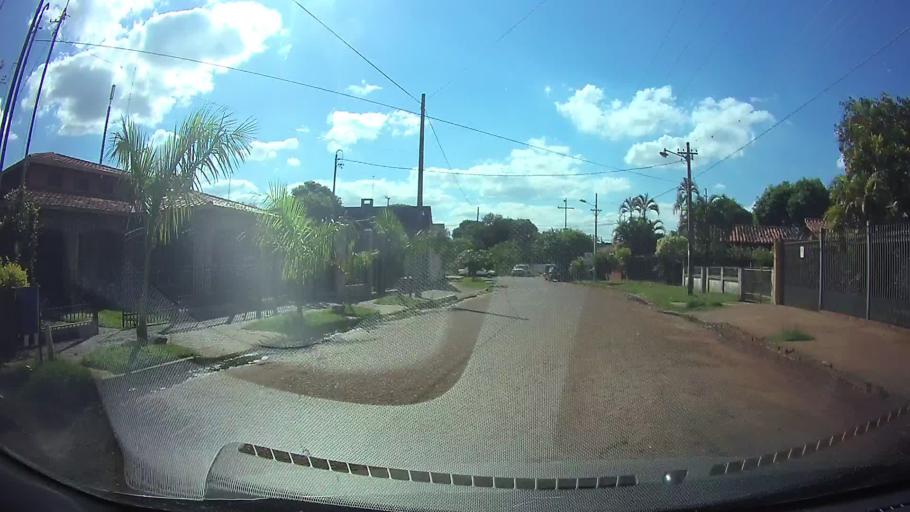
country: PY
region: Central
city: Itaugua
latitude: -25.3910
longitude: -57.3513
